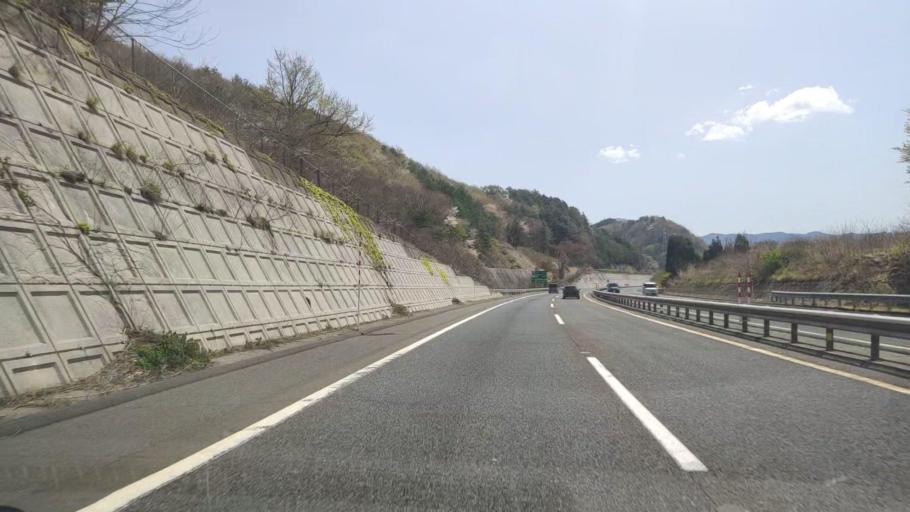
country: JP
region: Iwate
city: Ichinohe
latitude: 40.2292
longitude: 141.3201
